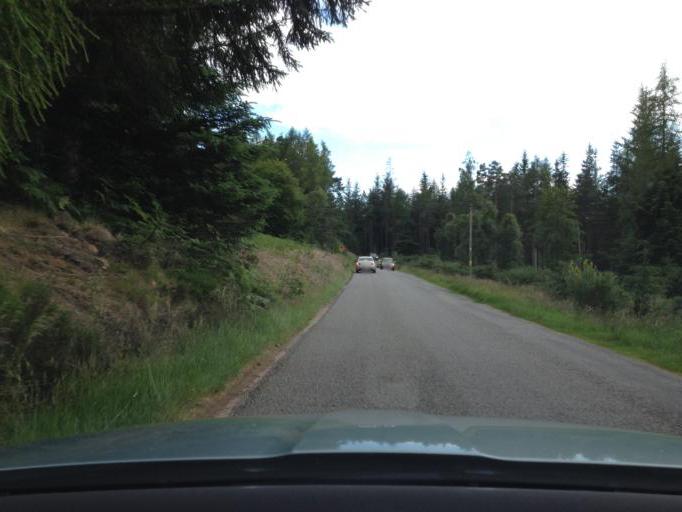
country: GB
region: Scotland
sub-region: Aberdeenshire
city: Banchory
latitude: 56.9853
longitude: -2.5753
